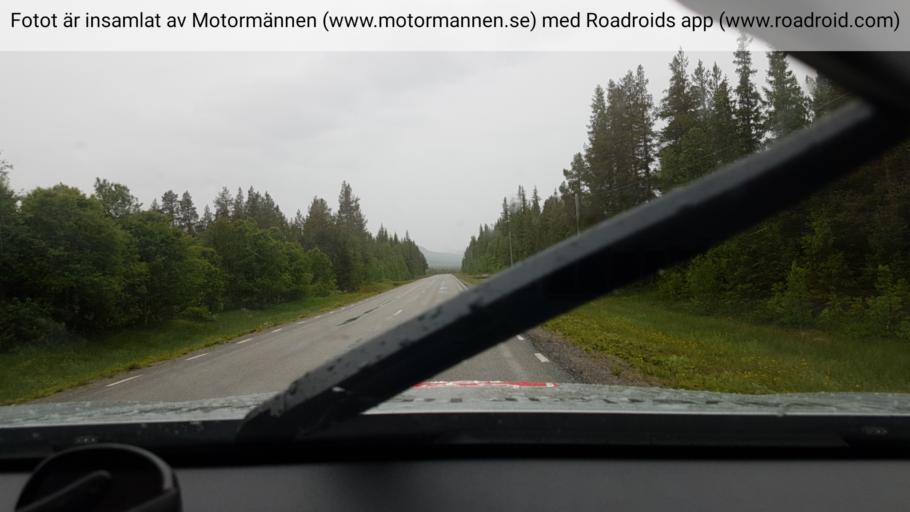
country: SE
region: Vaesterbotten
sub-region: Storumans Kommun
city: Fristad
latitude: 65.8690
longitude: 16.4276
